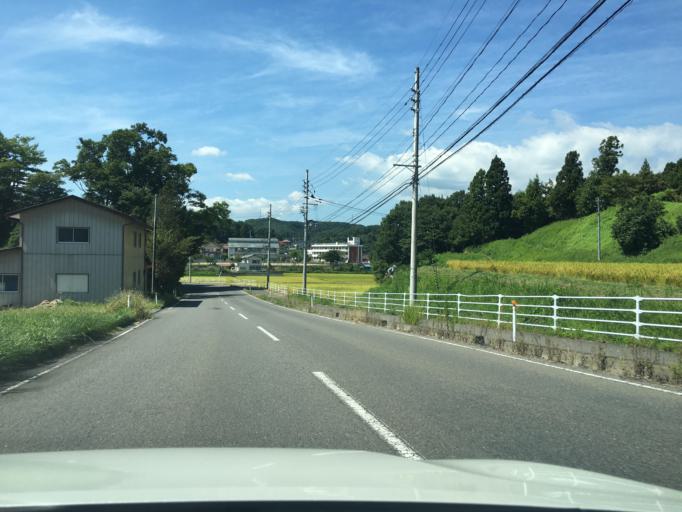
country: JP
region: Fukushima
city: Motomiya
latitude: 37.4931
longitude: 140.4333
